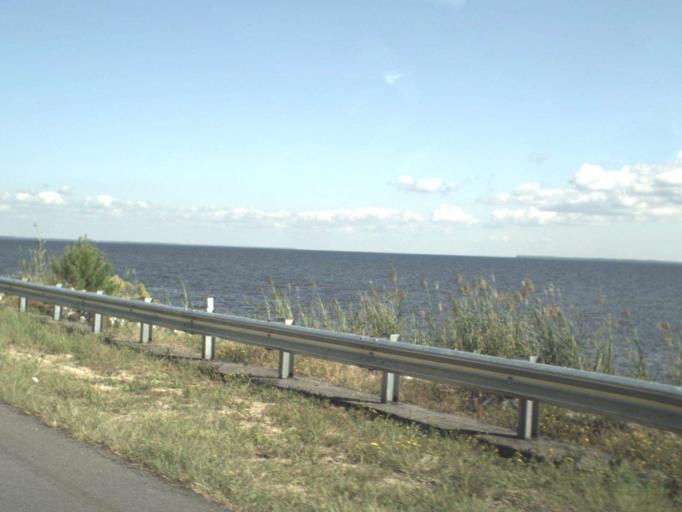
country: US
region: Florida
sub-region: Walton County
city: Miramar Beach
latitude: 30.4677
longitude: -86.3489
